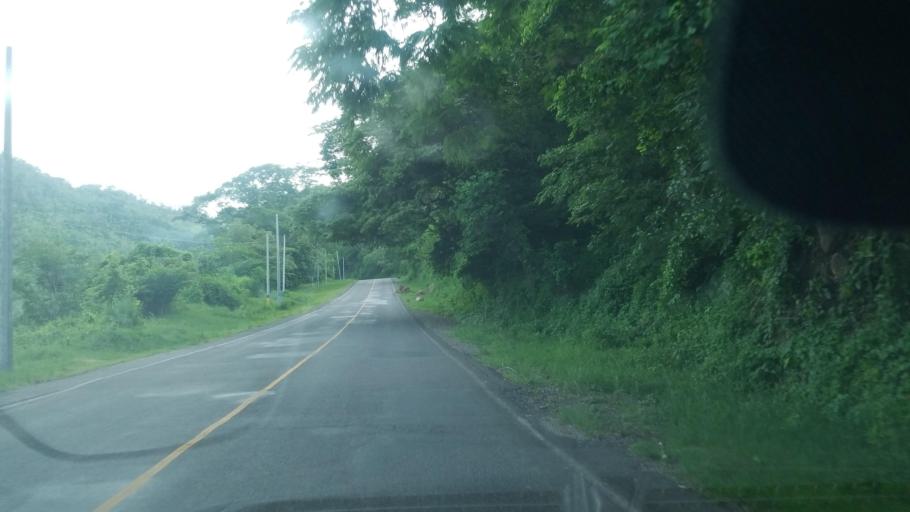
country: HN
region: Santa Barbara
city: Trinidad
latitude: 15.1146
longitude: -88.2033
